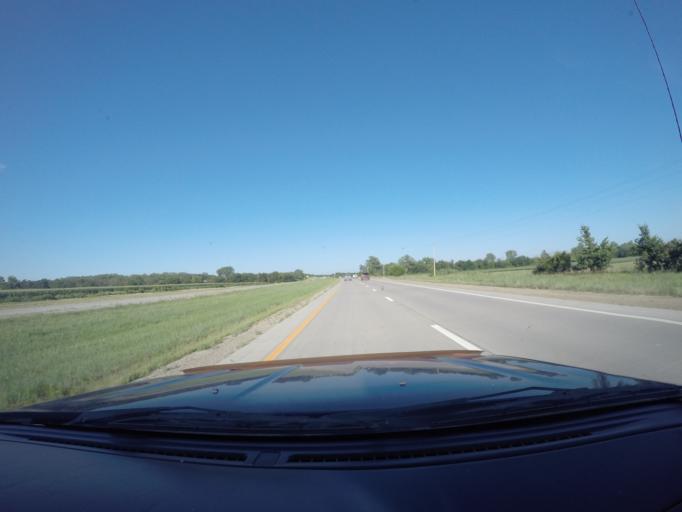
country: US
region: Kansas
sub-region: Shawnee County
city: Topeka
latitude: 39.0870
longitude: -95.5324
